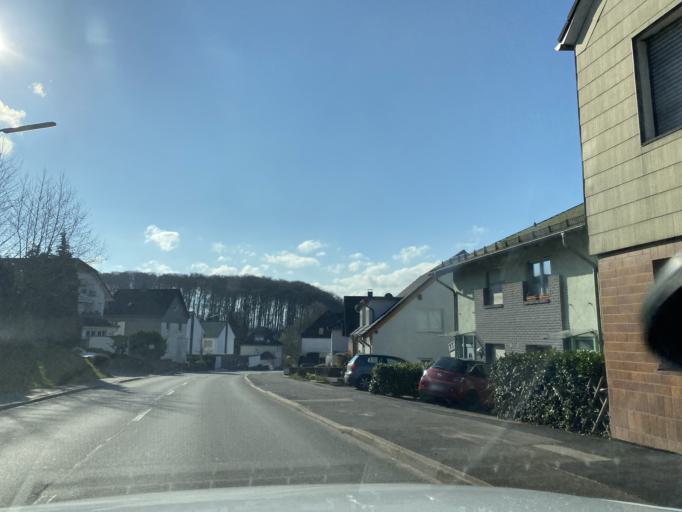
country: DE
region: North Rhine-Westphalia
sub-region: Regierungsbezirk Koln
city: Odenthal
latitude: 51.0144
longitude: 7.1248
